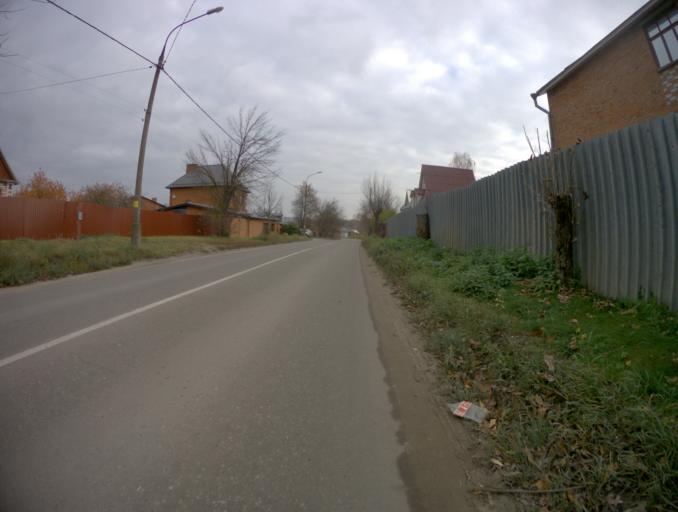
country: RU
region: Moskovskaya
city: Orekhovo-Zuyevo
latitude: 55.8205
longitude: 38.9807
